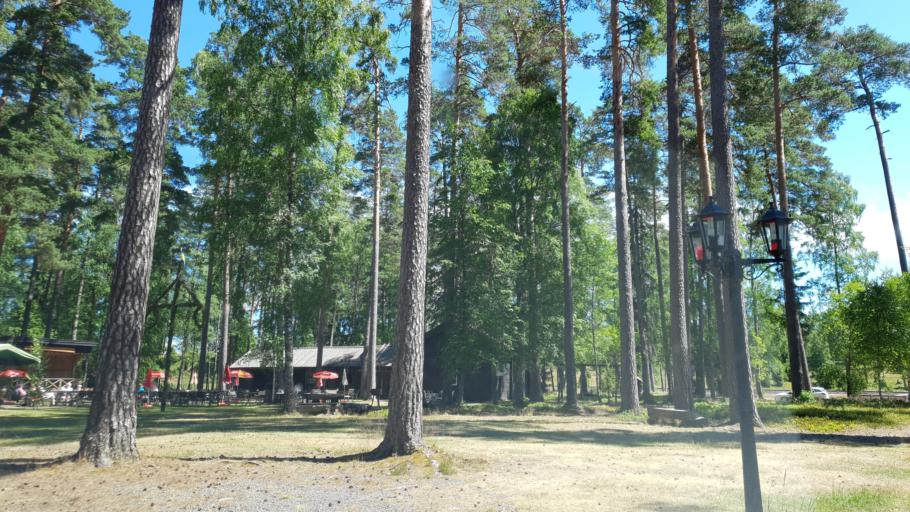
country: SE
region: Joenkoeping
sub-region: Vaggeryds Kommun
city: Vaggeryd
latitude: 57.5326
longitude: 14.1399
